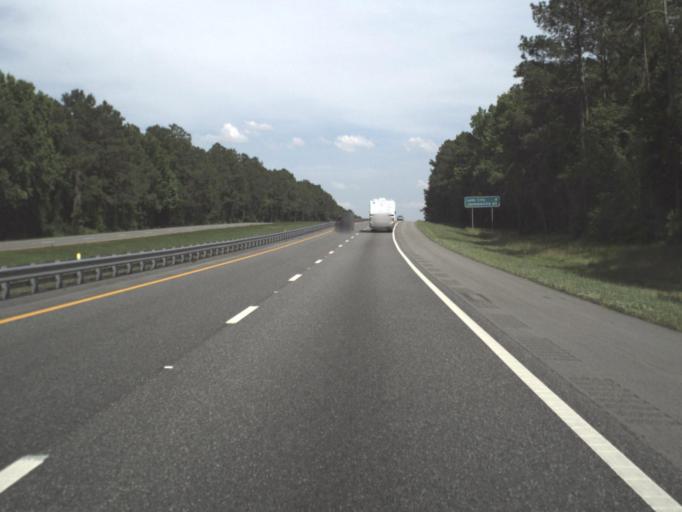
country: US
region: Florida
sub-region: Suwannee County
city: Wellborn
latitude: 30.2624
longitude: -82.7362
